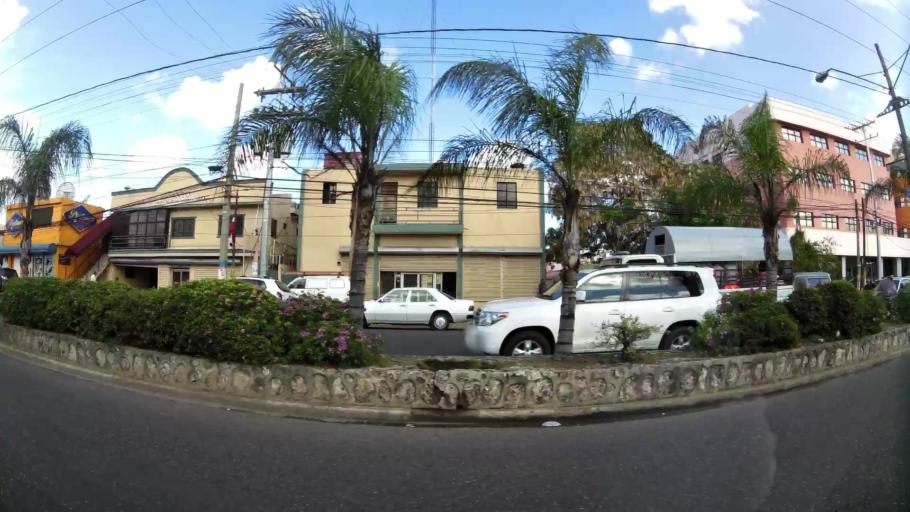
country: DO
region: Santo Domingo
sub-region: Santo Domingo
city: Santo Domingo Este
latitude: 18.5081
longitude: -69.8530
